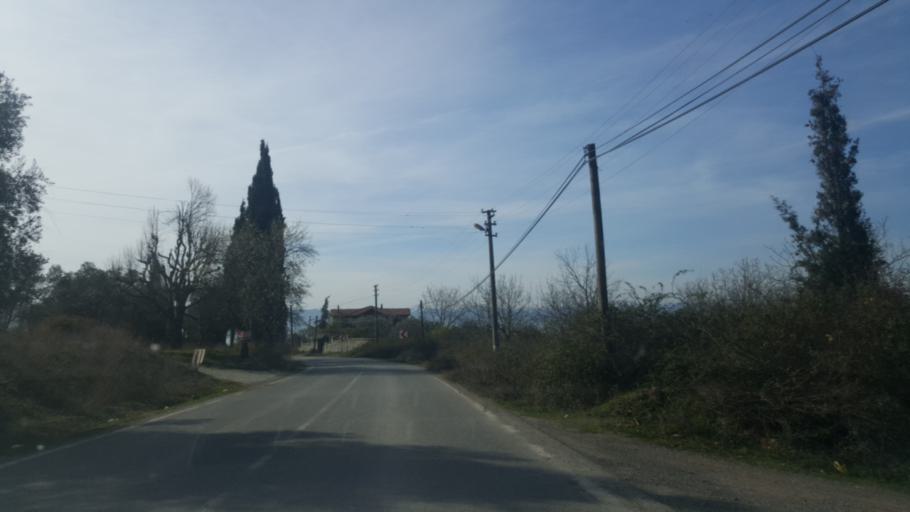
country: TR
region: Kocaeli
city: Tavsancil
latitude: 40.7788
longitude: 29.5750
